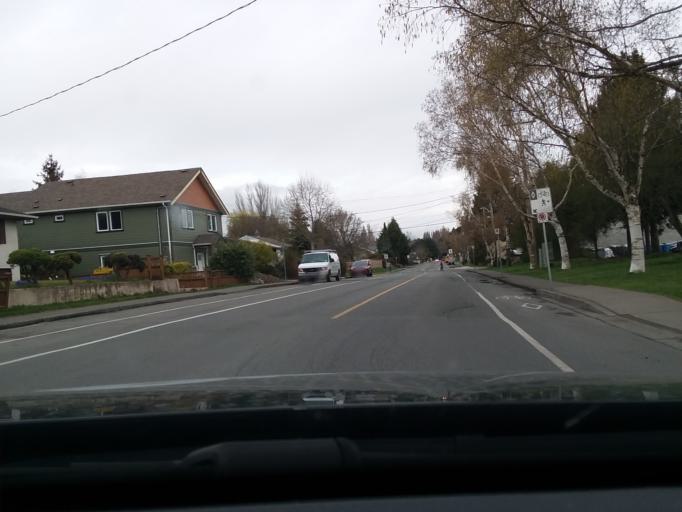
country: CA
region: British Columbia
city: Victoria
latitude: 48.4446
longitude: -123.3388
